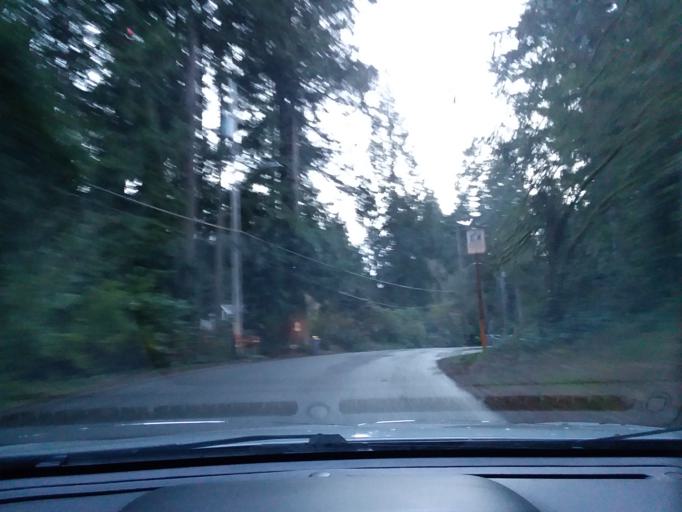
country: US
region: Washington
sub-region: King County
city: Lake Forest Park
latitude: 47.7585
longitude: -122.2878
